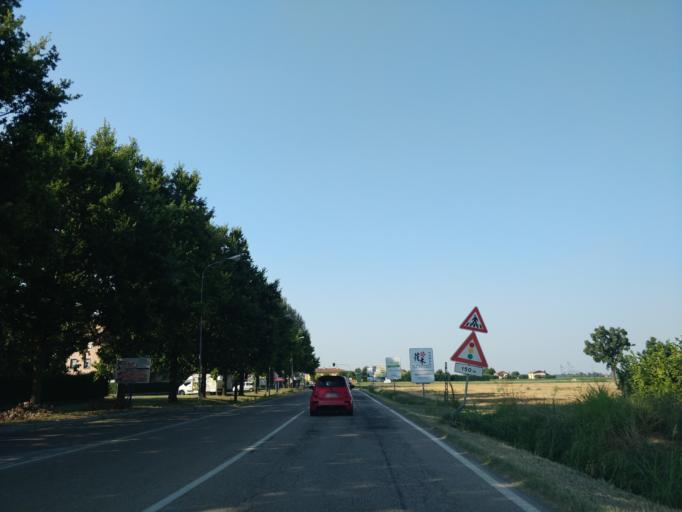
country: IT
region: Emilia-Romagna
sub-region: Provincia di Bologna
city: Castello d'Argile
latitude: 44.6777
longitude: 11.3000
